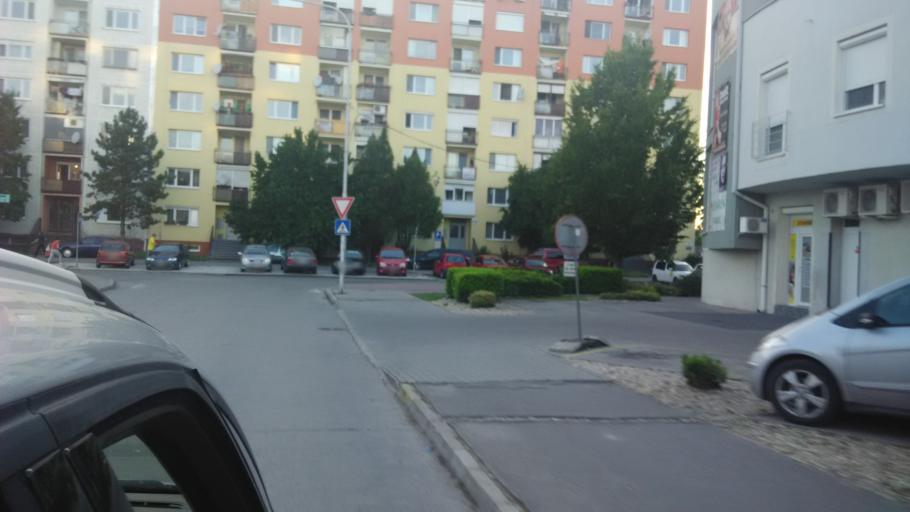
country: SK
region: Nitriansky
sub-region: Okres Nove Zamky
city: Nove Zamky
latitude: 47.9823
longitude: 18.1573
